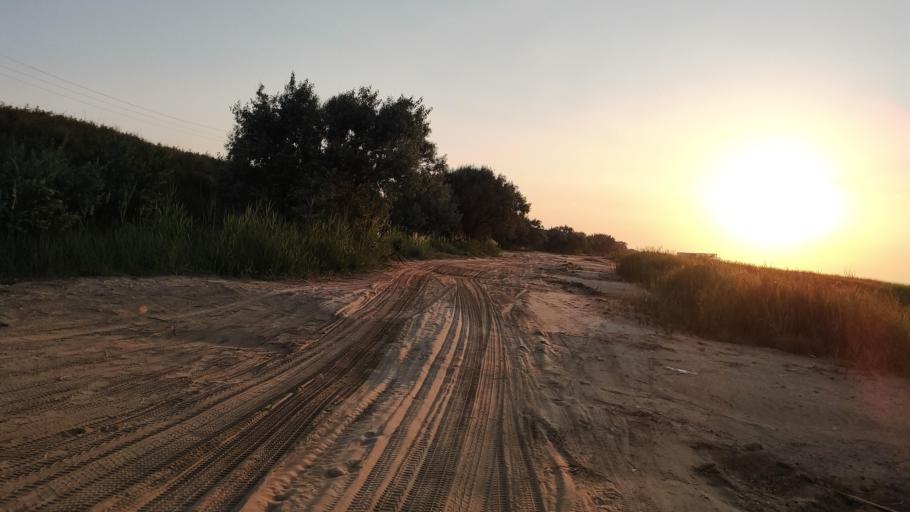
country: RU
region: Krasnodarskiy
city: Blagovetschenskaya
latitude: 45.0685
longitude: 37.0285
